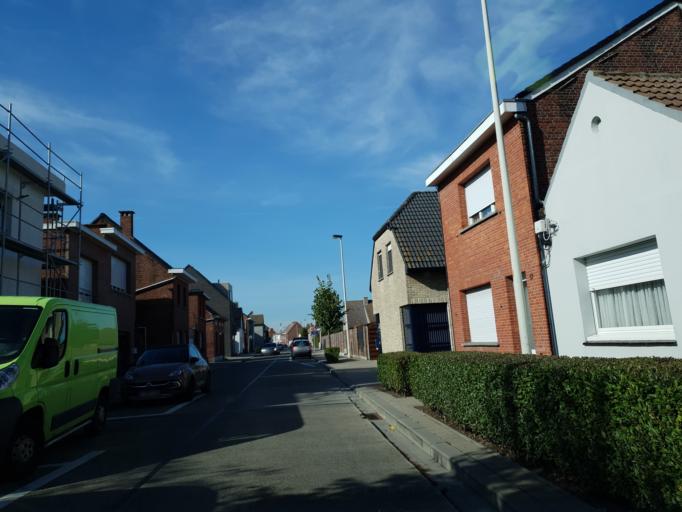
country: BE
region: Flanders
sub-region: Provincie Antwerpen
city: Stabroek
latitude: 51.3582
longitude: 4.3207
